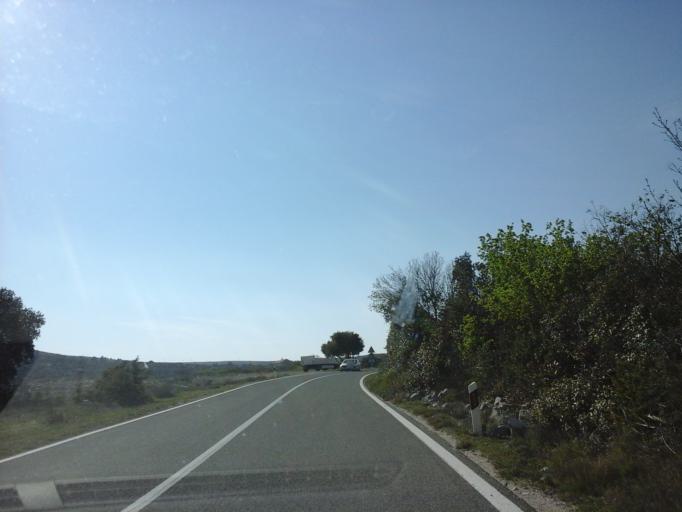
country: HR
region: Splitsko-Dalmatinska
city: Bol
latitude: 43.3180
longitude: 16.7015
